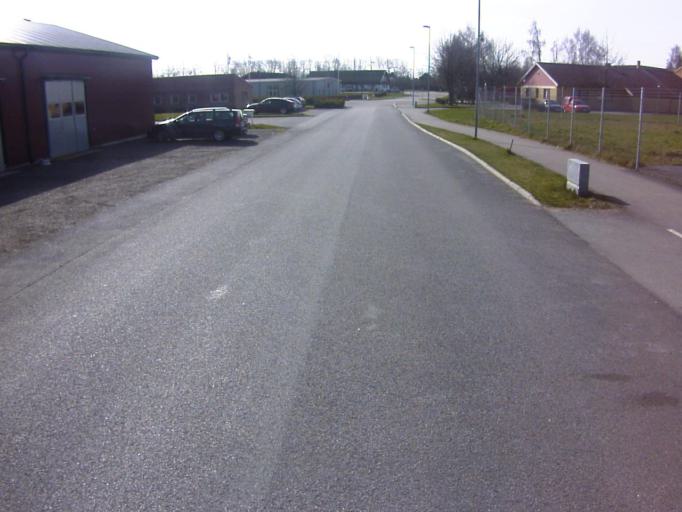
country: SE
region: Skane
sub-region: Kavlinge Kommun
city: Kaevlinge
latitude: 55.7999
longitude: 13.1192
